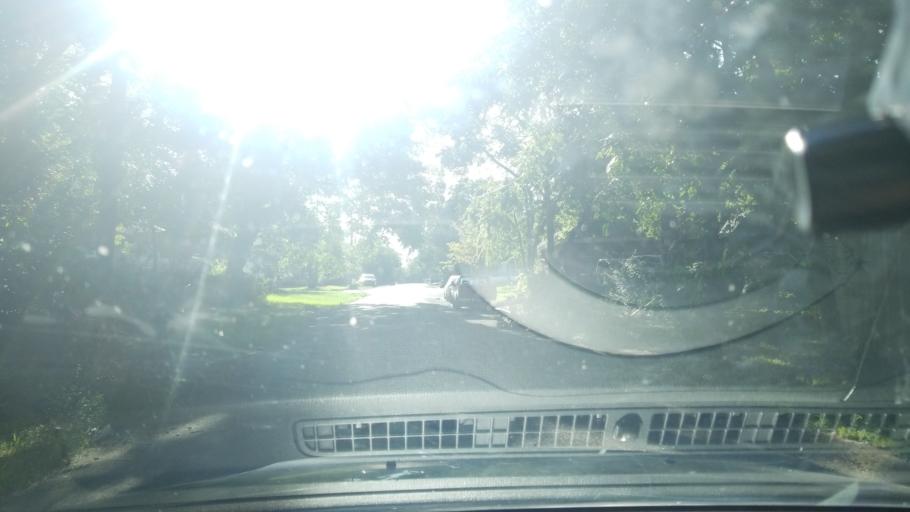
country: US
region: Texas
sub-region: Dallas County
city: Dallas
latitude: 32.7277
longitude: -96.8176
